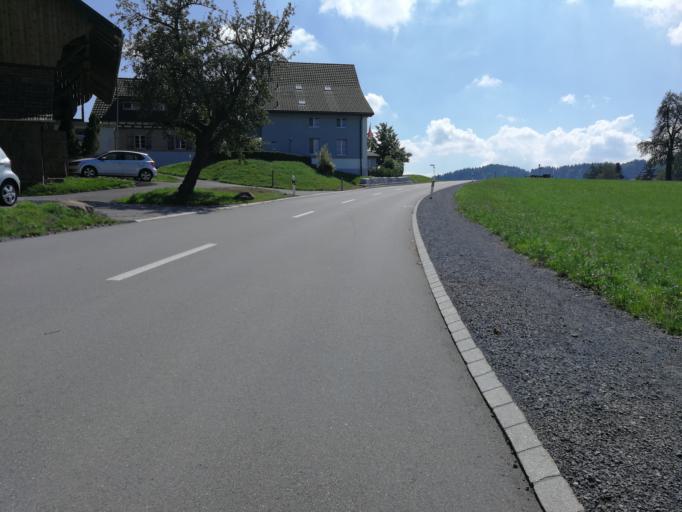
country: CH
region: Zurich
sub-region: Bezirk Horgen
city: Au / Unter-Dorf
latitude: 47.2358
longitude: 8.6277
